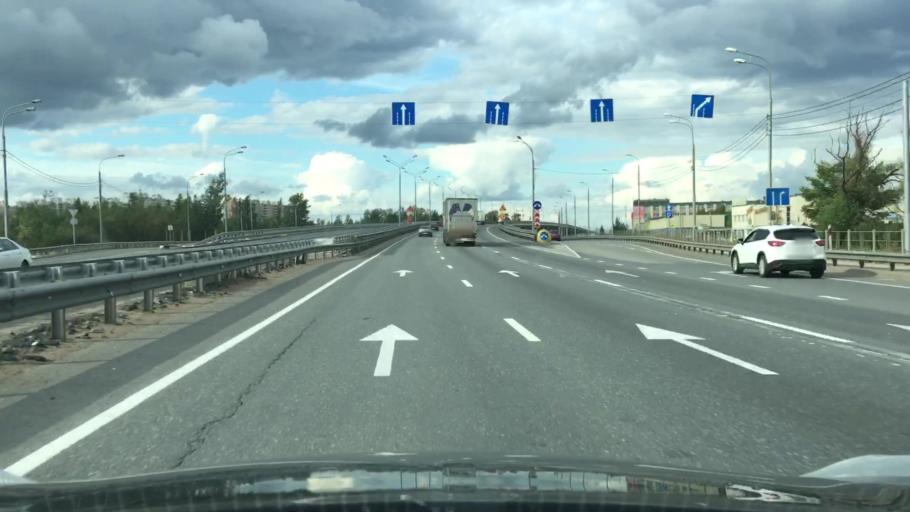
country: RU
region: Tverskaya
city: Tver
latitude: 56.8389
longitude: 35.7942
